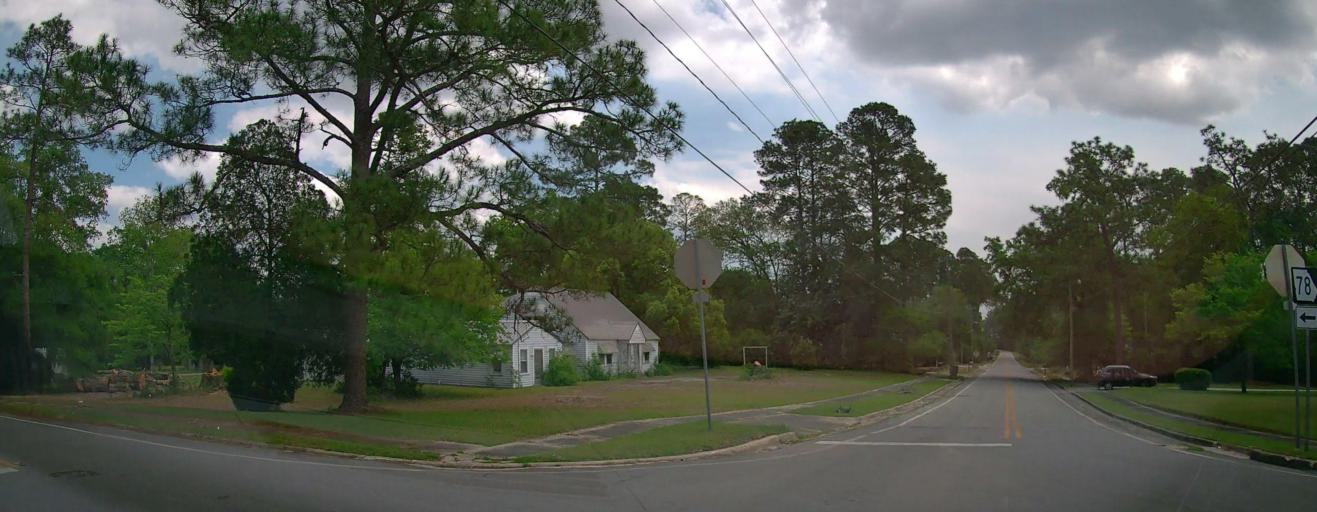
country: US
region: Georgia
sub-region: Treutlen County
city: Soperton
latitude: 32.3748
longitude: -82.5856
